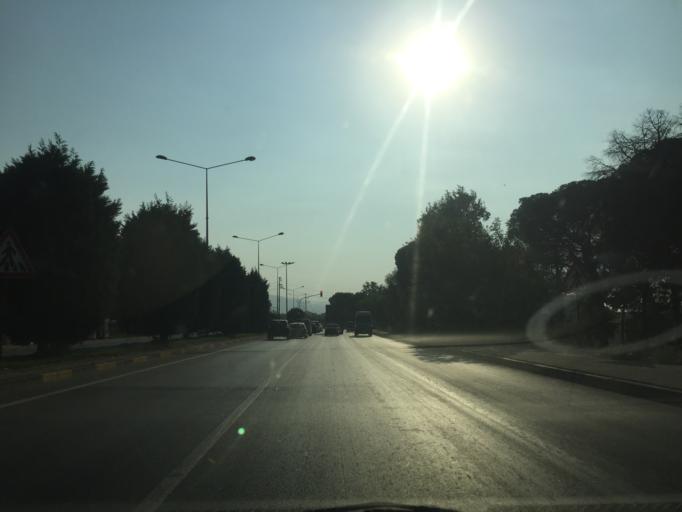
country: TR
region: Manisa
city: Salihli
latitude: 38.4909
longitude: 28.1631
